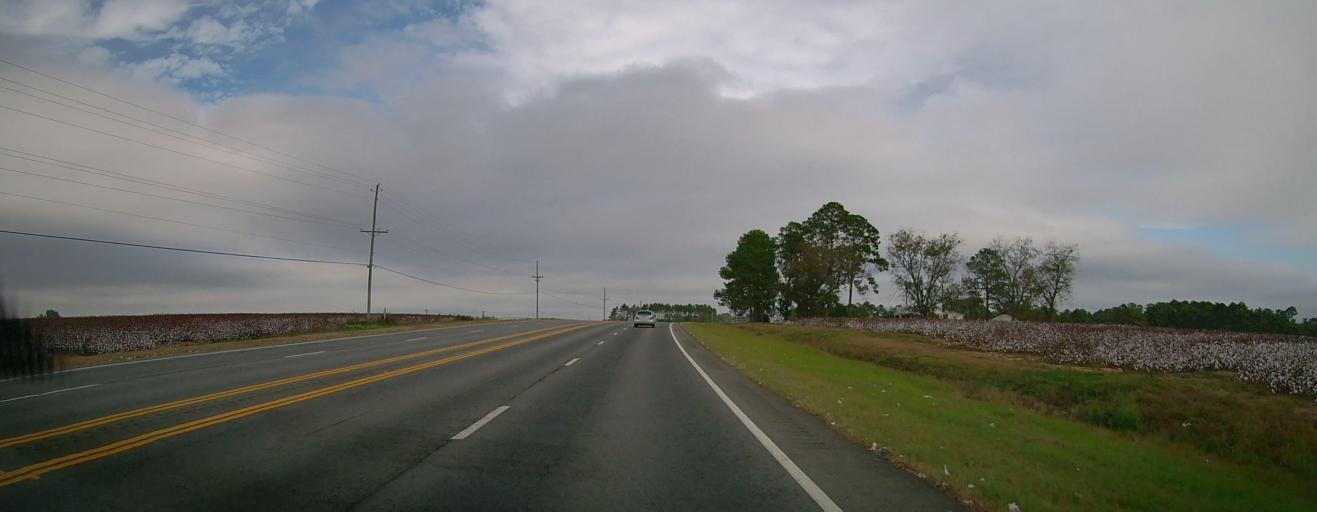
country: US
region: Georgia
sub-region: Tift County
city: Omega
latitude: 31.3676
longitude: -83.5731
